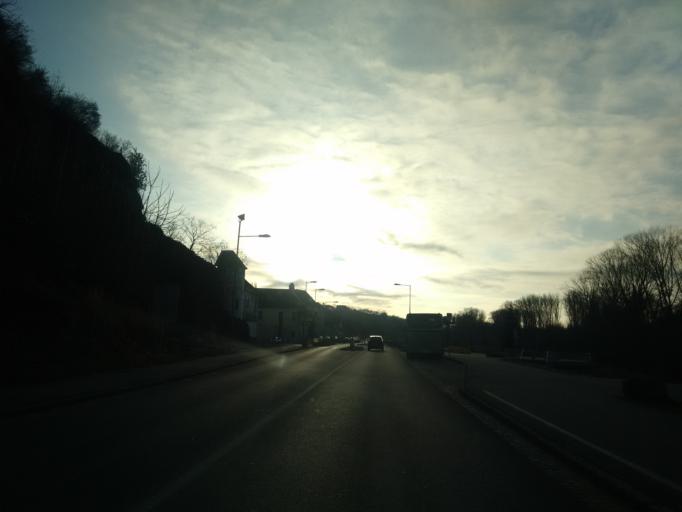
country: AT
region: Lower Austria
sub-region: Politischer Bezirk Melk
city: Melk
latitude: 48.2286
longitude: 15.3294
